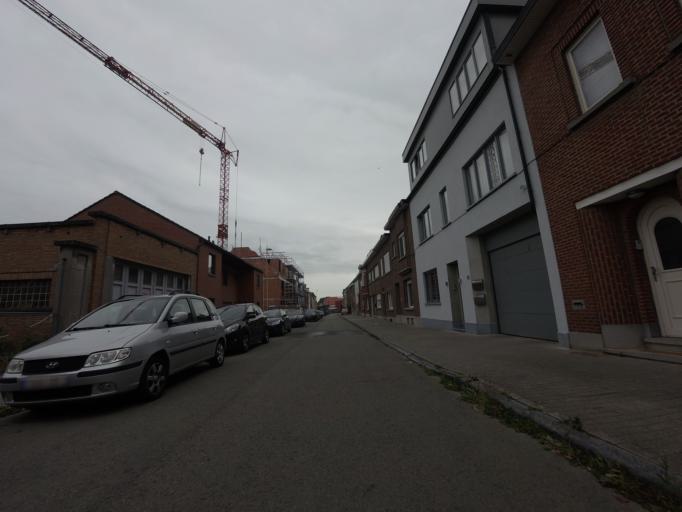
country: BE
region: Flanders
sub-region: Provincie Vlaams-Brabant
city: Grimbergen
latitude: 50.9374
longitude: 4.3647
